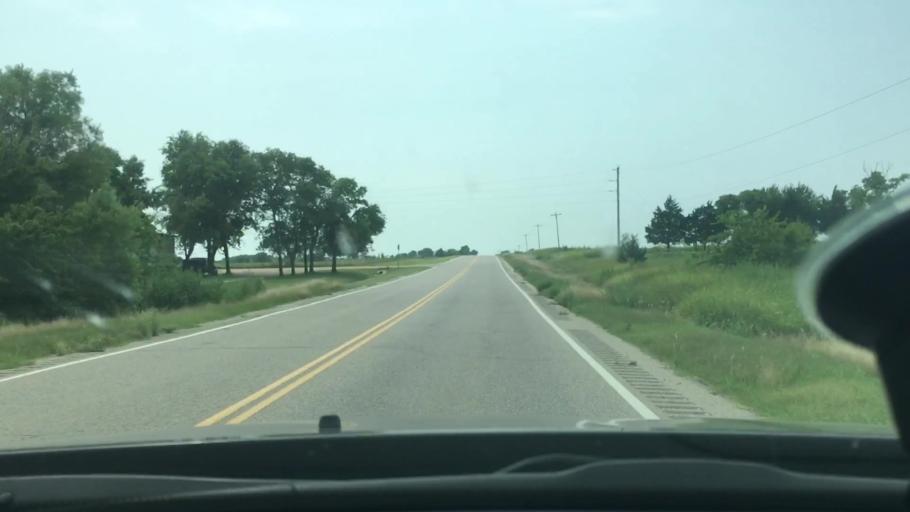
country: US
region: Oklahoma
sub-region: Marshall County
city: Madill
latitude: 34.0430
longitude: -96.7611
